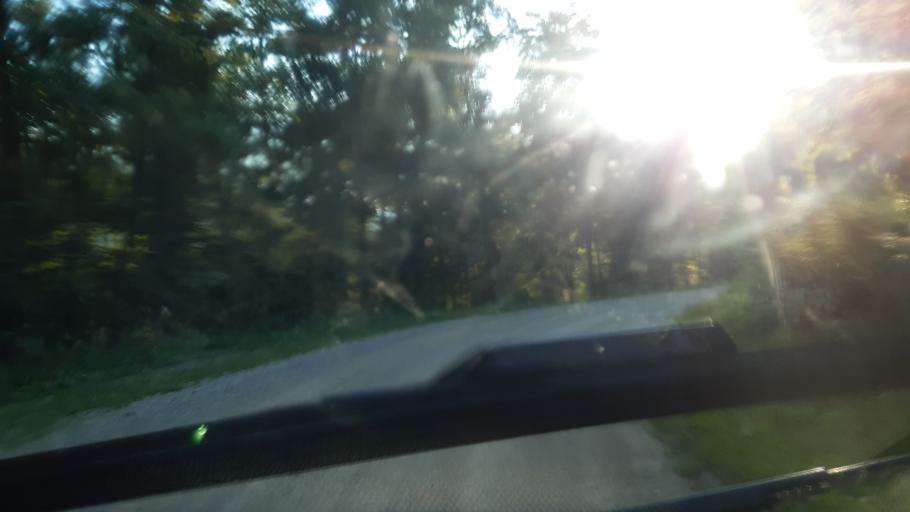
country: SI
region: Kocevje
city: Kocevje
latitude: 45.6664
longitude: 14.9588
